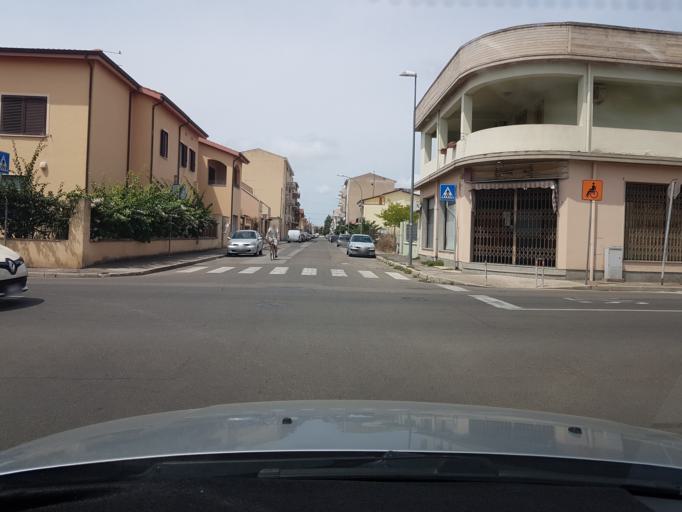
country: IT
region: Sardinia
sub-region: Provincia di Oristano
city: Oristano
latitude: 39.9099
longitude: 8.5964
